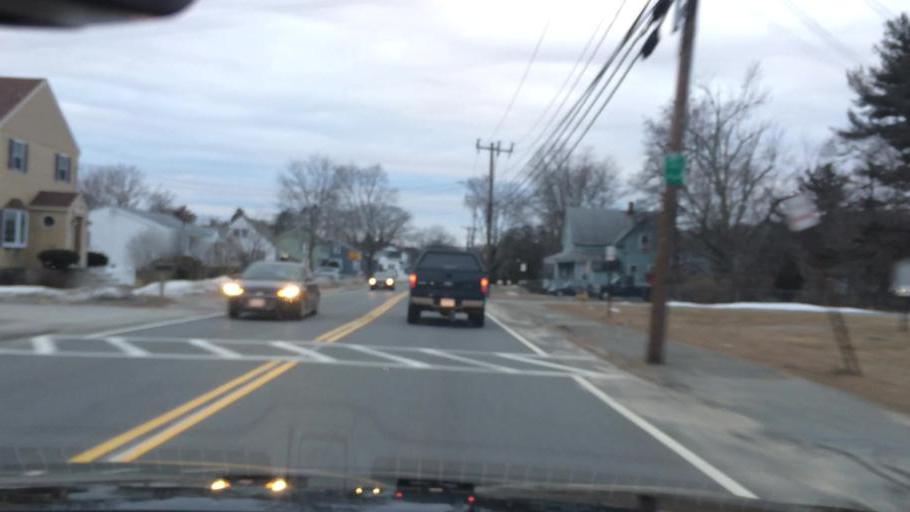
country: US
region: Massachusetts
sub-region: Essex County
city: North Andover
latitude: 42.7459
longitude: -71.1319
